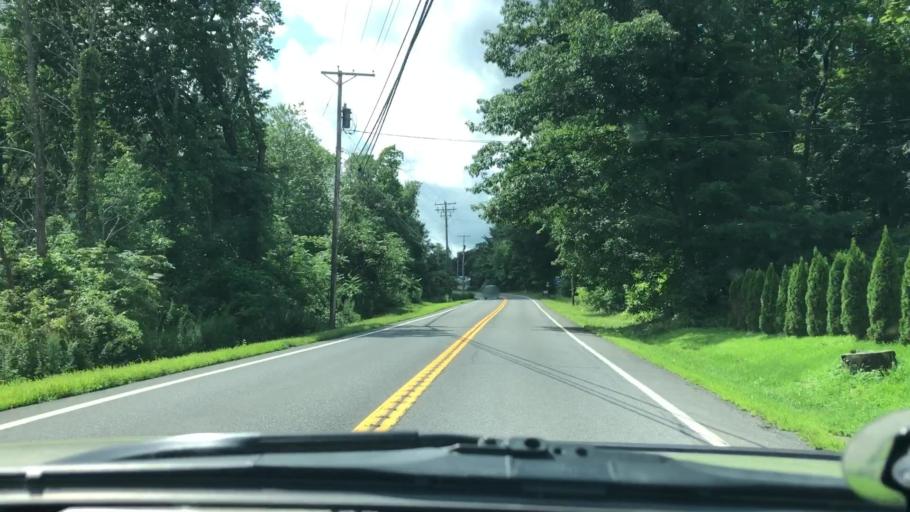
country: US
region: New York
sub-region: Ulster County
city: Manorville
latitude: 42.1388
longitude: -74.0011
